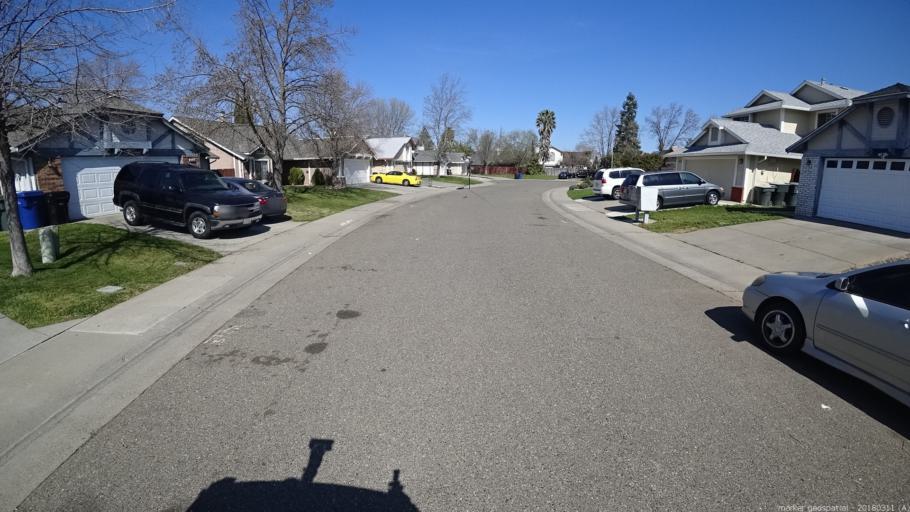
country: US
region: California
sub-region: Sacramento County
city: Florin
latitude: 38.4621
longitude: -121.3932
